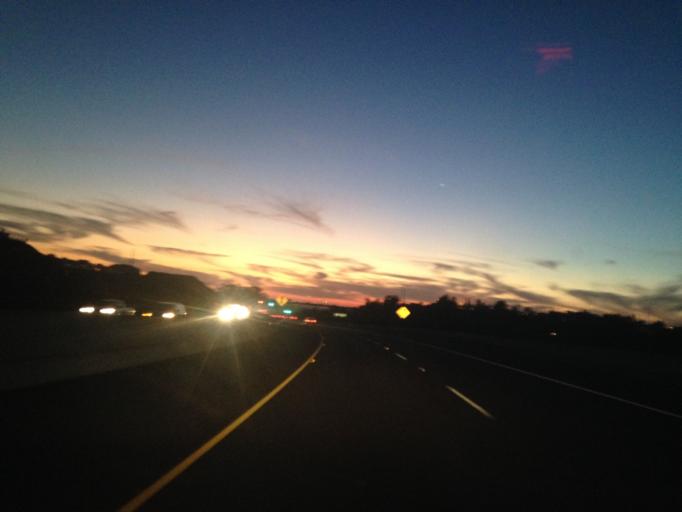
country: US
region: California
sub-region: San Diego County
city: Oceanside
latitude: 33.2120
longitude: -117.3755
